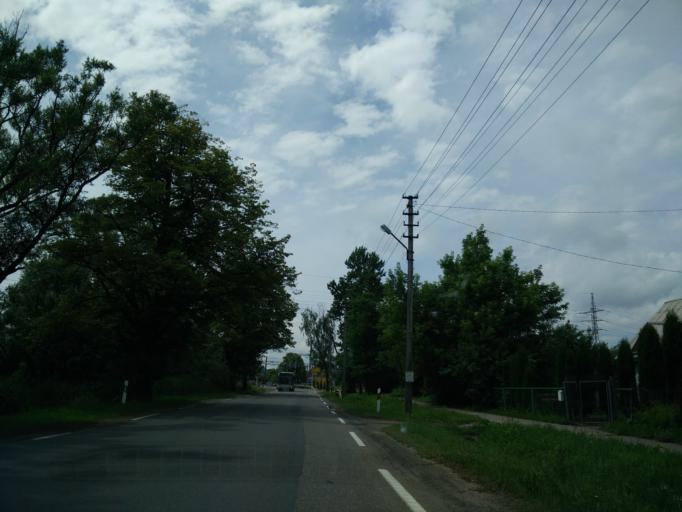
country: LT
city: Skaidiskes
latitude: 54.6936
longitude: 25.4518
